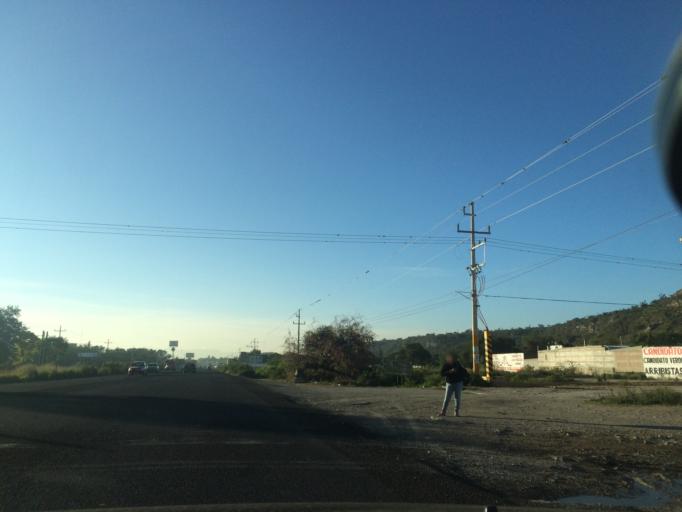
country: MX
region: Puebla
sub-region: Santiago Miahuatlan
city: San Jose Monte Chiquito
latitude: 18.4815
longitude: -97.4464
